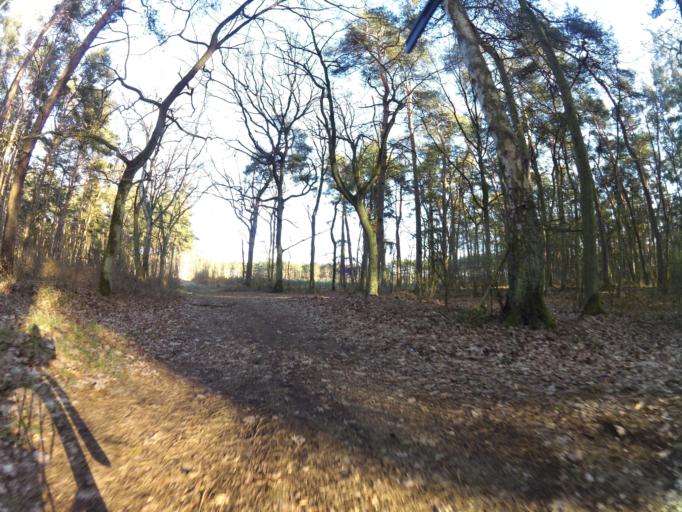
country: PL
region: West Pomeranian Voivodeship
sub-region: Powiat policki
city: Nowe Warpno
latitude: 53.7340
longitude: 14.3136
